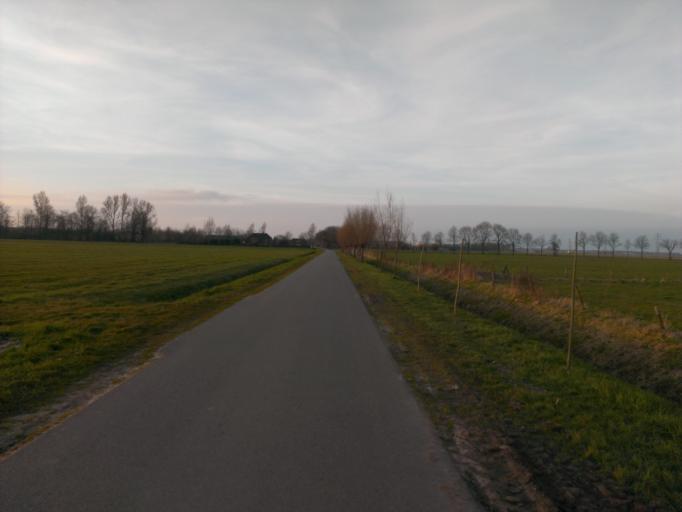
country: NL
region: Gelderland
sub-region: Gemeente Heerde
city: Heerde
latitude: 52.4054
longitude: 6.0812
